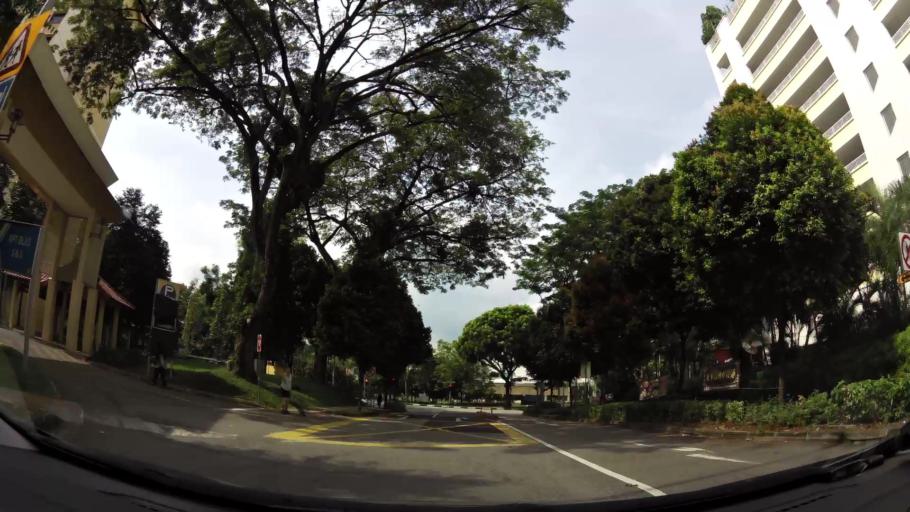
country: SG
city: Singapore
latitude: 1.3042
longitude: 103.7821
